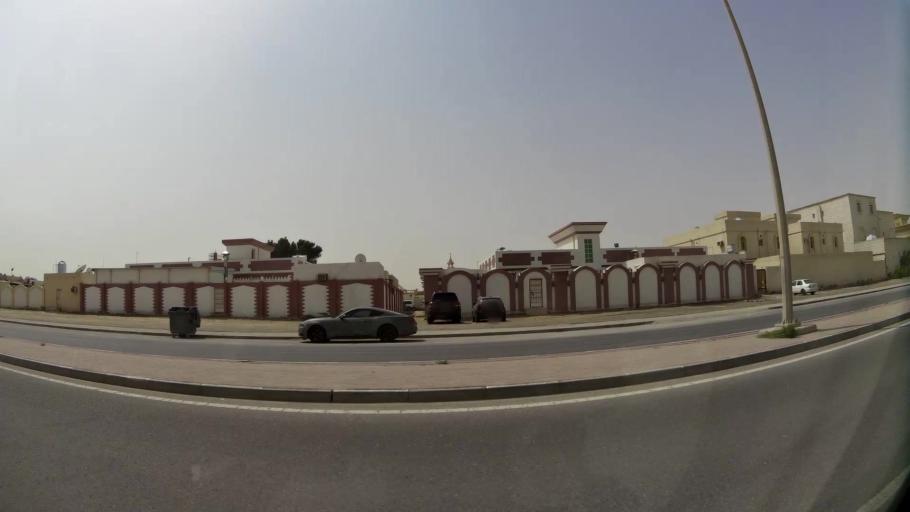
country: QA
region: Baladiyat ar Rayyan
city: Ar Rayyan
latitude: 25.2369
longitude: 51.4204
